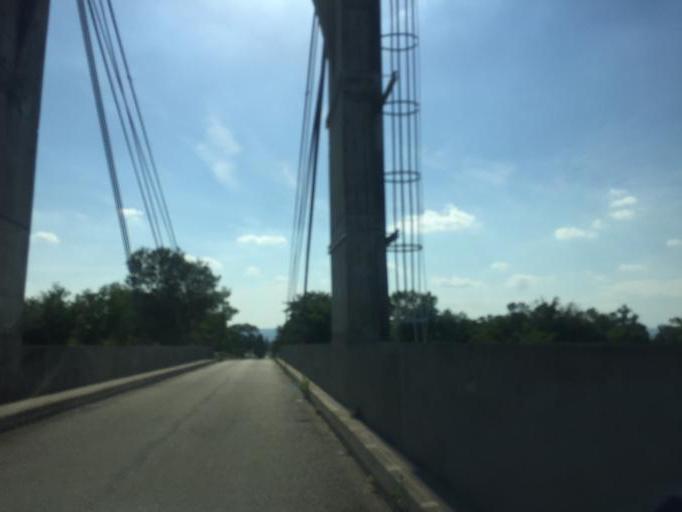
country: FR
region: Rhone-Alpes
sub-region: Departement de la Drome
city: Pierrelatte
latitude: 44.3823
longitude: 4.7280
